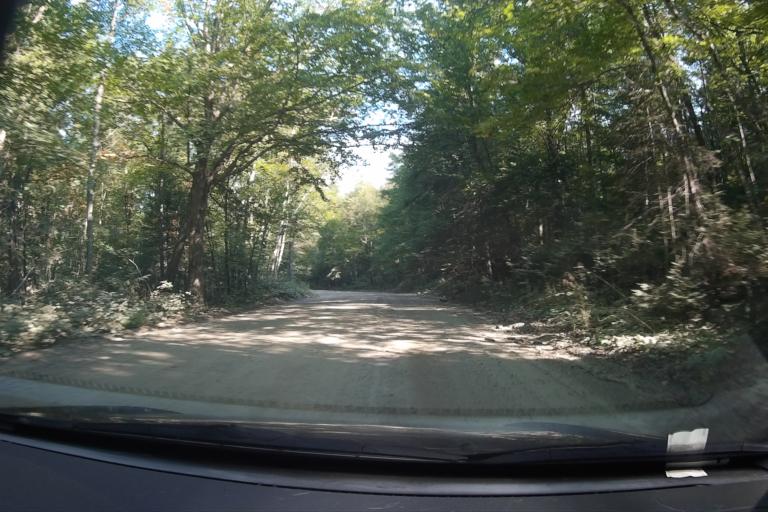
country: CA
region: Ontario
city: Huntsville
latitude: 45.5607
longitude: -78.6960
